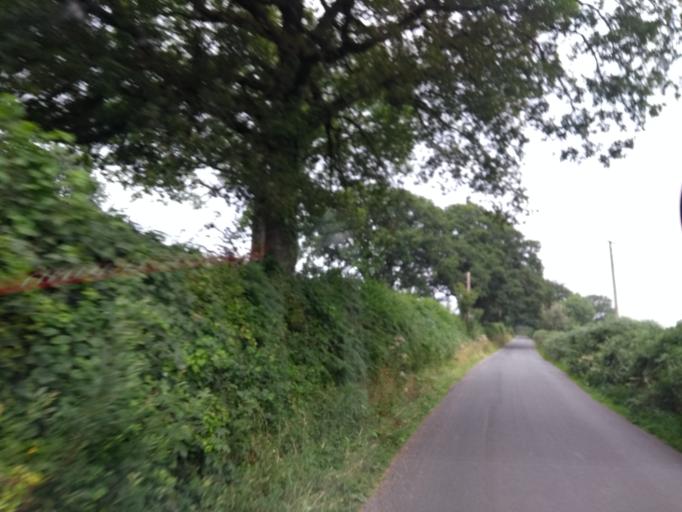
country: GB
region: England
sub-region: Somerset
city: Chard
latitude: 50.8726
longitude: -3.0797
